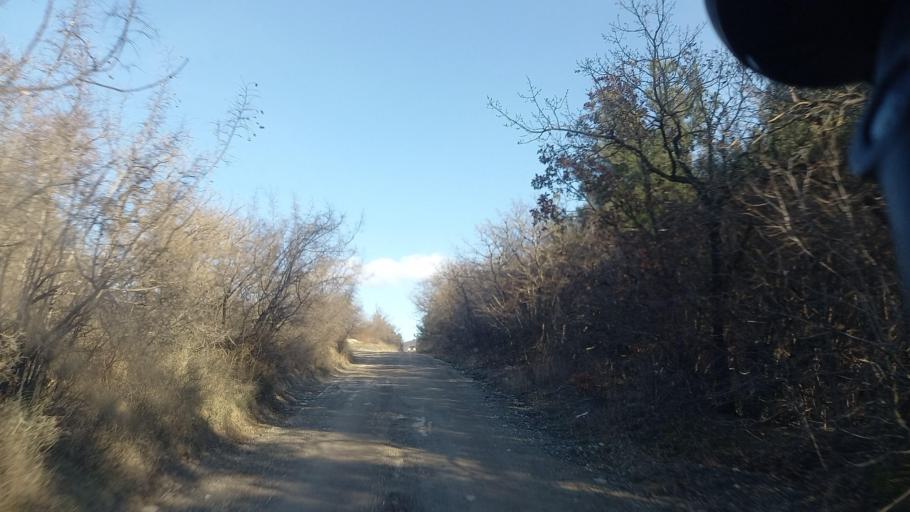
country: RU
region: Krasnodarskiy
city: Kabardinka
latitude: 44.6296
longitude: 37.9206
